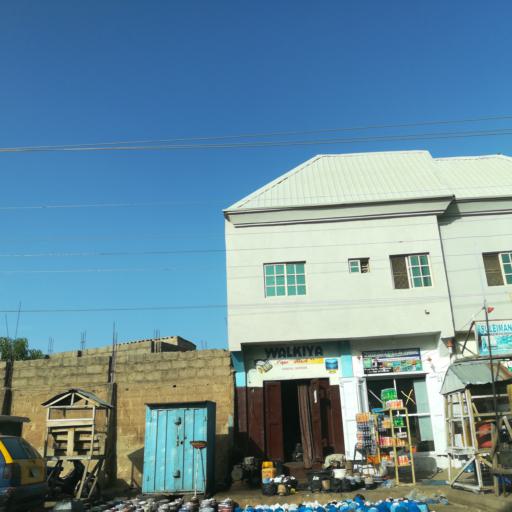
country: NG
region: Kano
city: Kano
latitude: 12.0159
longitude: 8.4960
